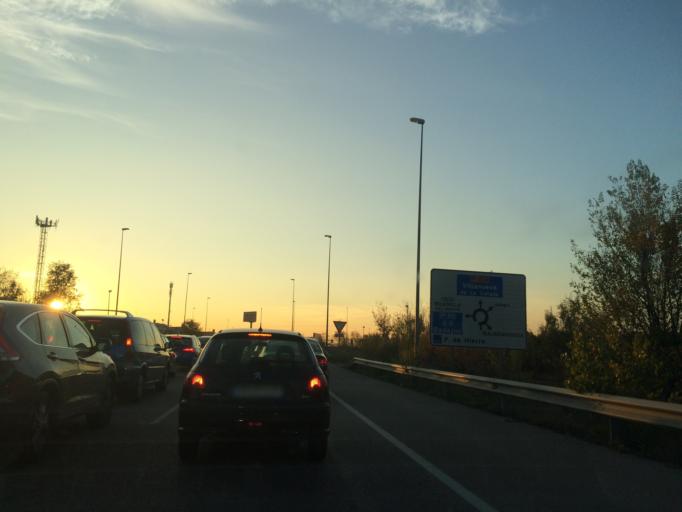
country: ES
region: Madrid
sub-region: Provincia de Madrid
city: Majadahonda
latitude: 40.4541
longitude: -3.8774
